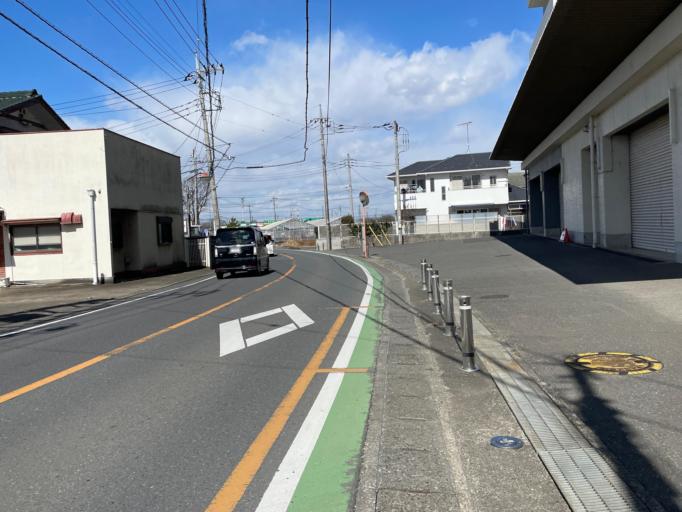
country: JP
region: Saitama
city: Sakado
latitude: 35.9767
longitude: 139.4169
